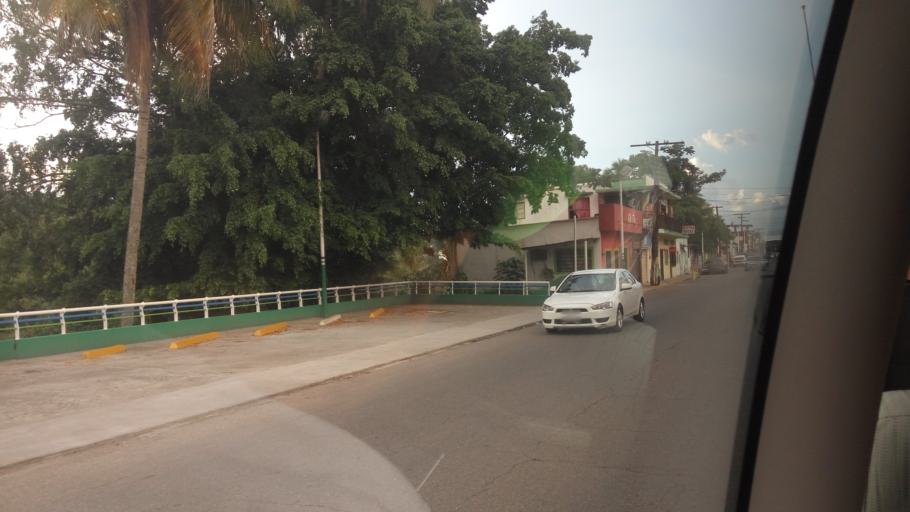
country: MX
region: Tabasco
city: Teapa
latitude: 17.5572
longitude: -92.9504
